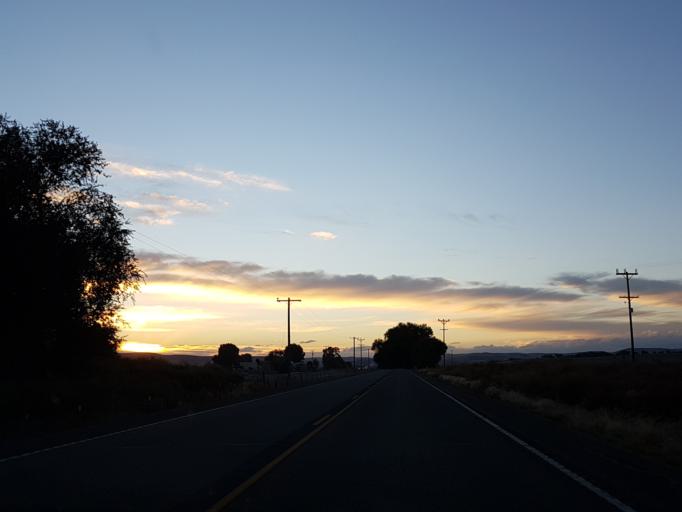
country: US
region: Oregon
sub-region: Malheur County
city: Vale
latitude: 43.9384
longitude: -117.3297
